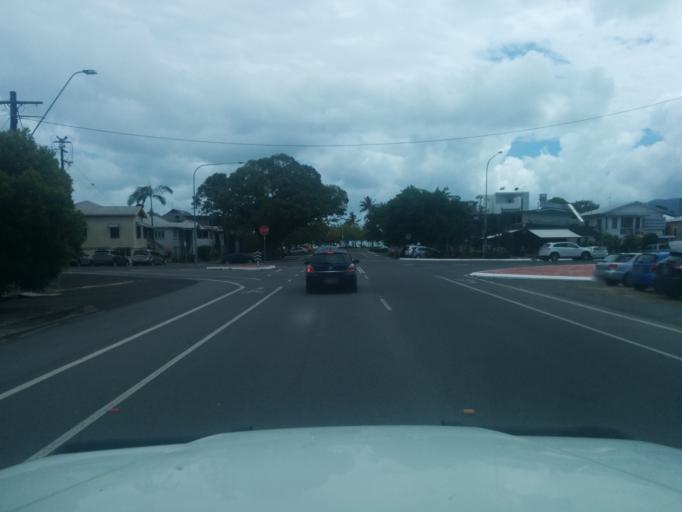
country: AU
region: Queensland
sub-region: Cairns
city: Cairns
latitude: -16.9109
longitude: 145.7655
